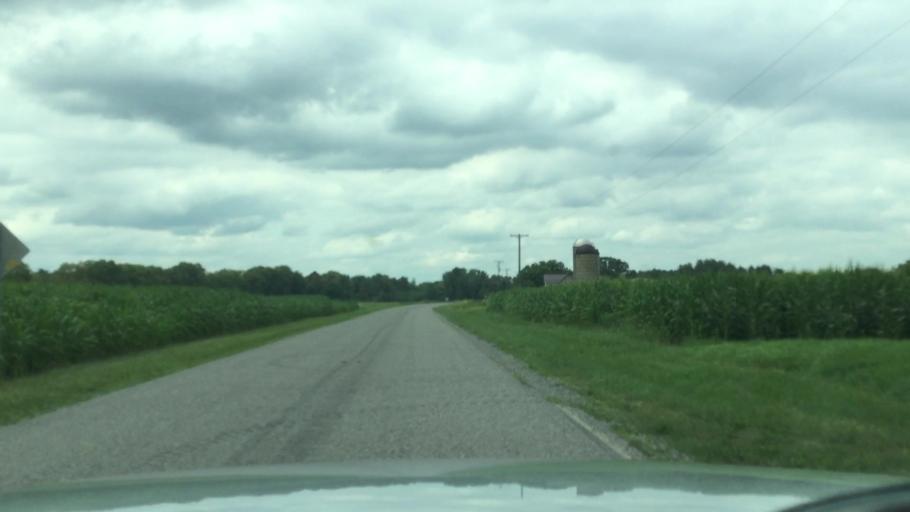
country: US
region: Michigan
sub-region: Saginaw County
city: Burt
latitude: 43.2572
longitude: -83.8725
